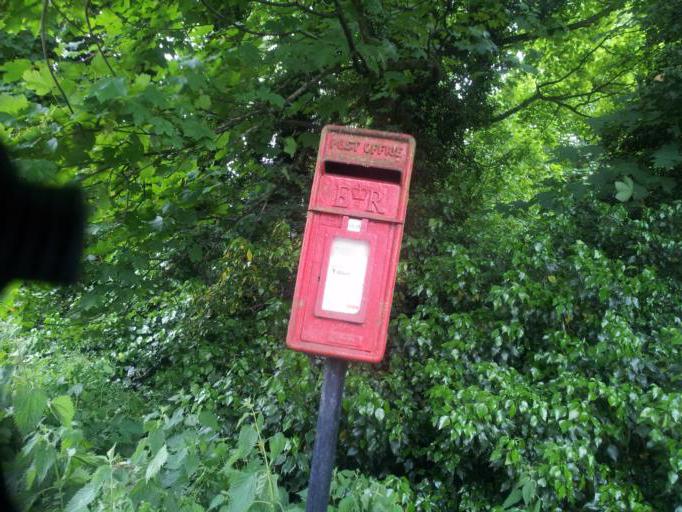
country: GB
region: England
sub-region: Kent
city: Maidstone
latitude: 51.2964
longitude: 0.5100
